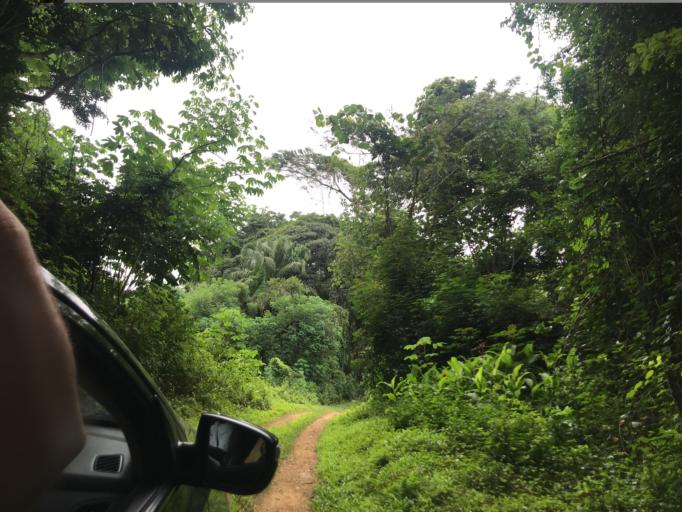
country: AO
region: Cuanza Norte
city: N'dalatando
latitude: -9.0739
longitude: 14.8074
